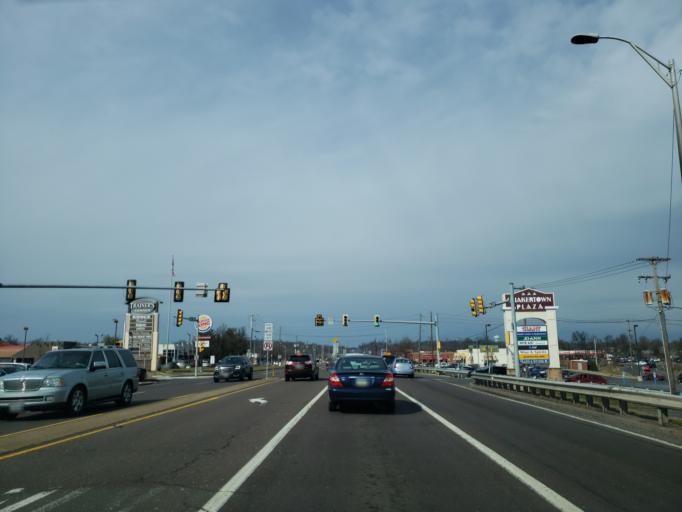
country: US
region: Pennsylvania
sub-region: Bucks County
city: Quakertown
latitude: 40.4457
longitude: -75.3595
